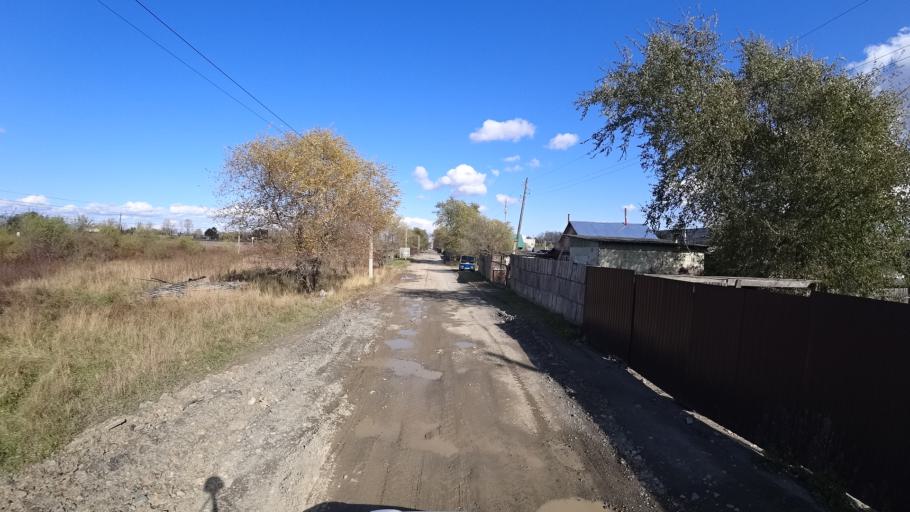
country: RU
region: Khabarovsk Krai
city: Amursk
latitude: 50.0954
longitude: 136.5043
